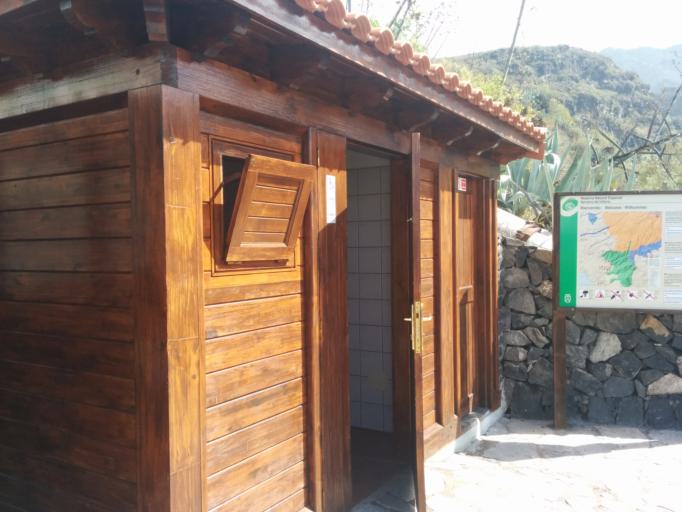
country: ES
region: Canary Islands
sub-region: Provincia de Santa Cruz de Tenerife
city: Adeje
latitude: 28.1263
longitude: -16.7236
